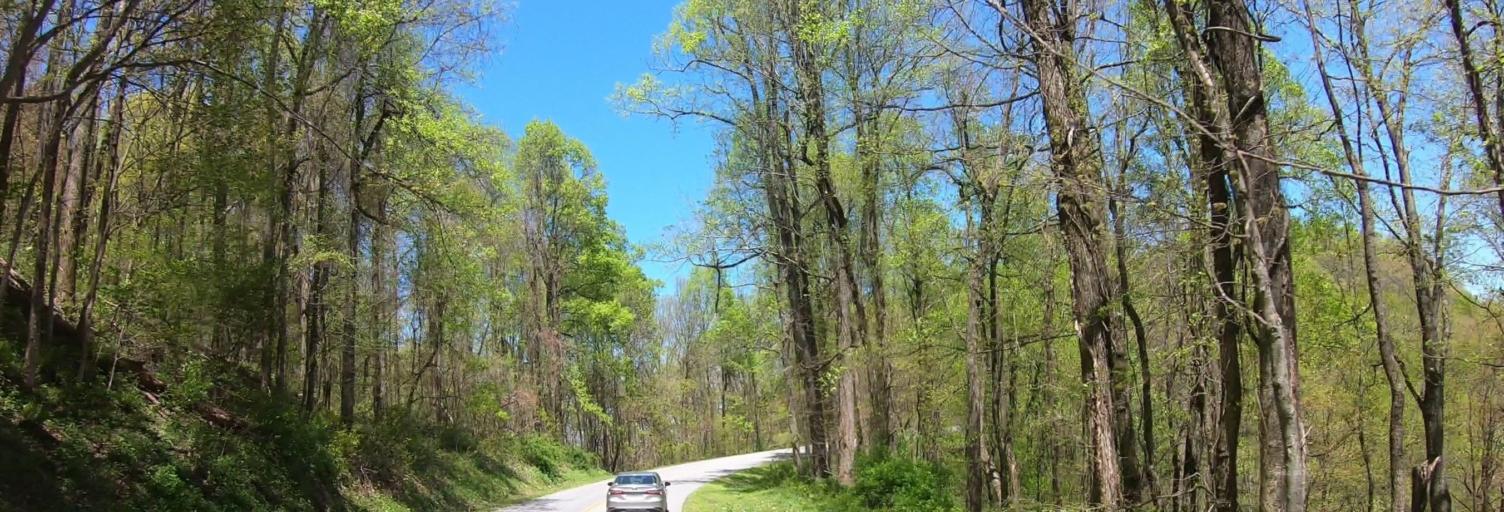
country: US
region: North Carolina
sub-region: Buncombe County
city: Avery Creek
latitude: 35.4703
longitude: -82.6198
